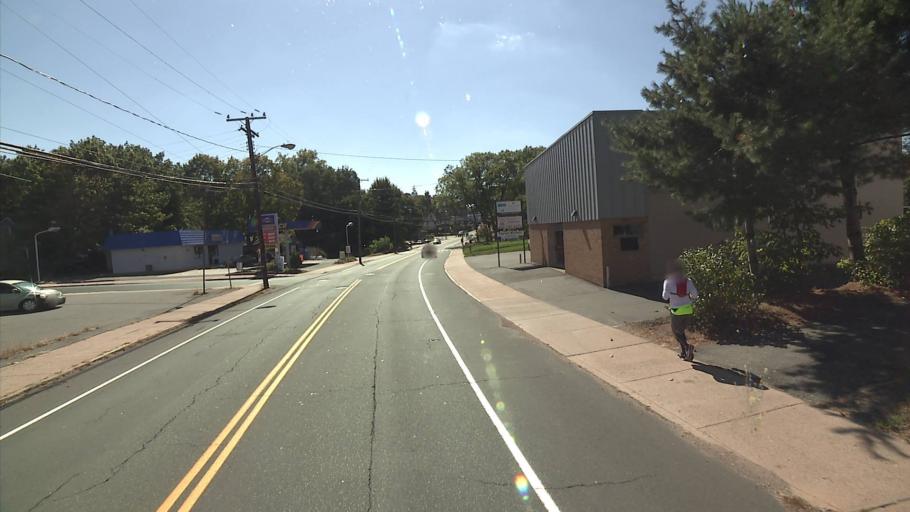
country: US
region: Connecticut
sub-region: Hartford County
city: Manchester
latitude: 41.7802
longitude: -72.5217
